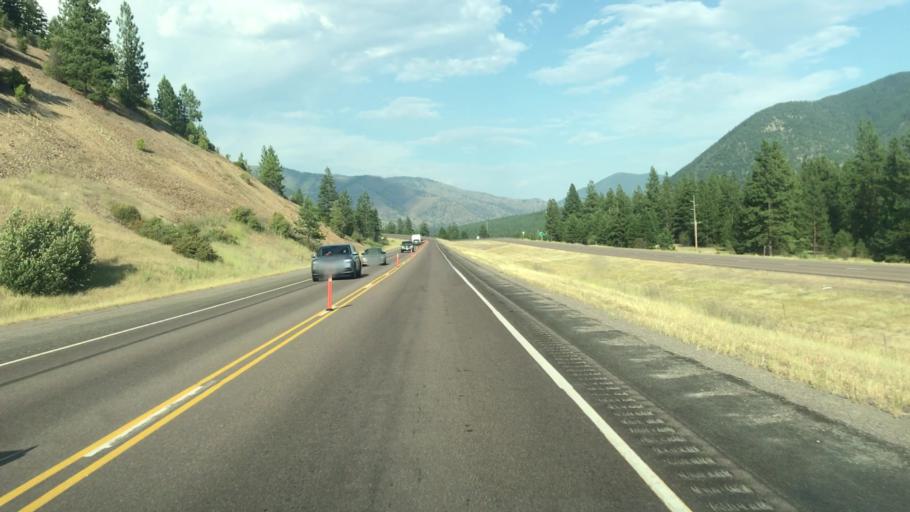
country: US
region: Montana
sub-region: Mineral County
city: Superior
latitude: 47.0128
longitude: -114.7038
